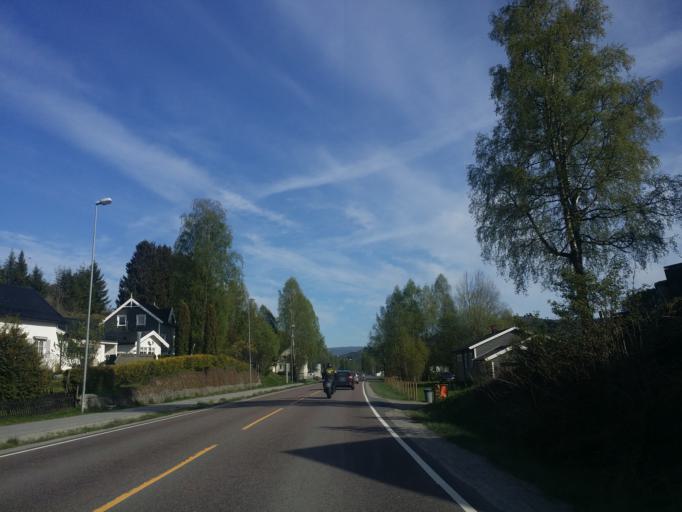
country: NO
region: Telemark
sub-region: Notodden
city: Notodden
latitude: 59.5747
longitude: 9.1960
